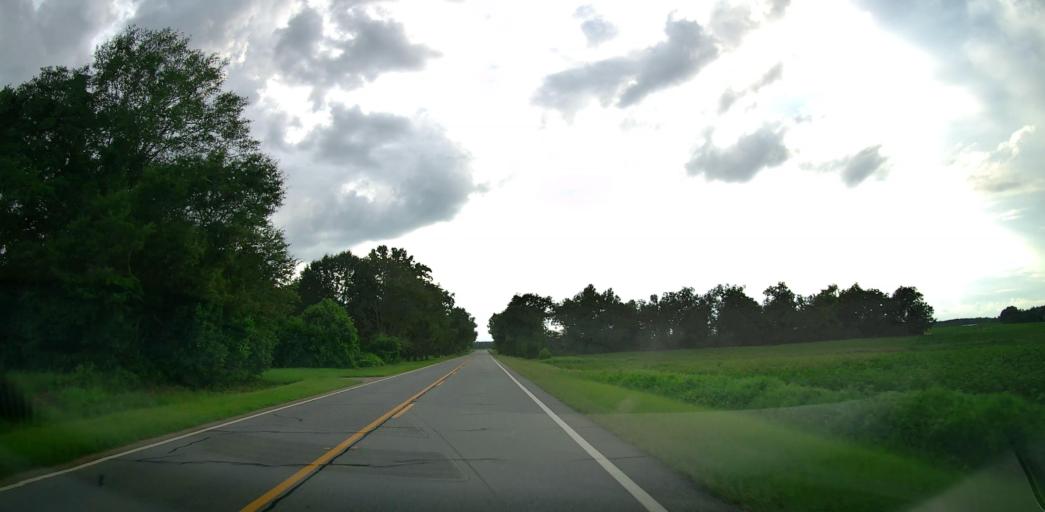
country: US
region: Georgia
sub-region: Pulaski County
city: Hawkinsville
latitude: 32.2959
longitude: -83.5283
